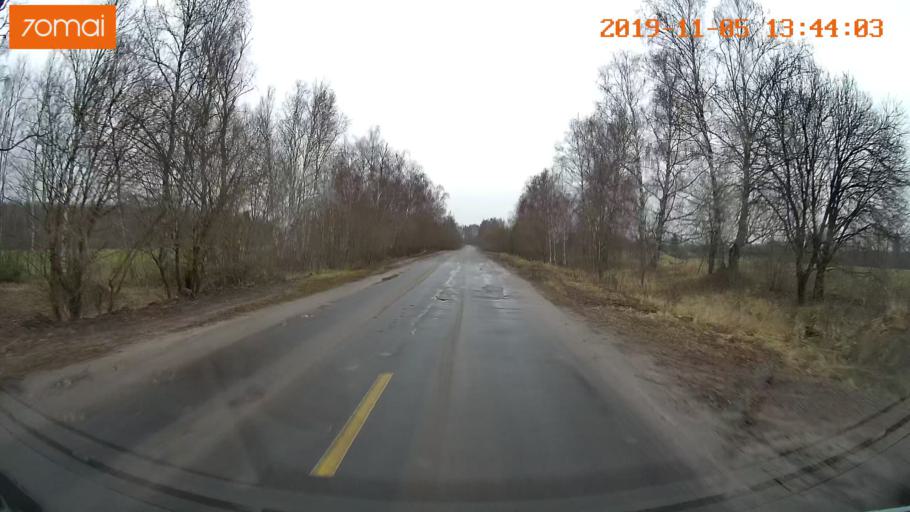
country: RU
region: Ivanovo
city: Shuya
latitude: 56.9781
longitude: 41.4079
